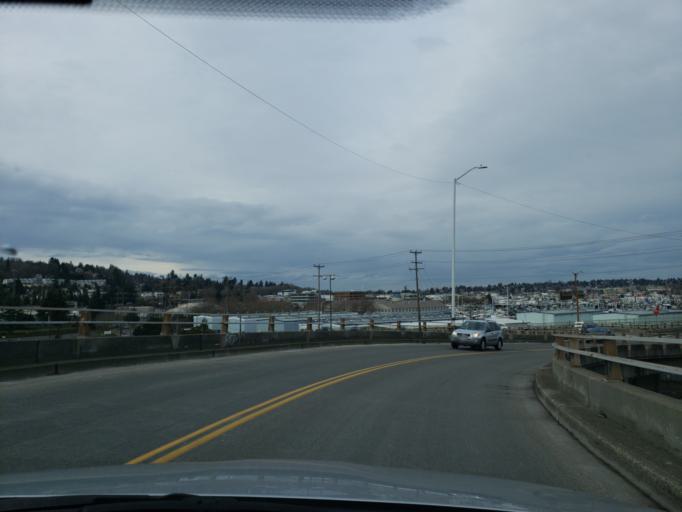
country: US
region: Washington
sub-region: King County
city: Seattle
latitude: 47.6532
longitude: -122.3770
